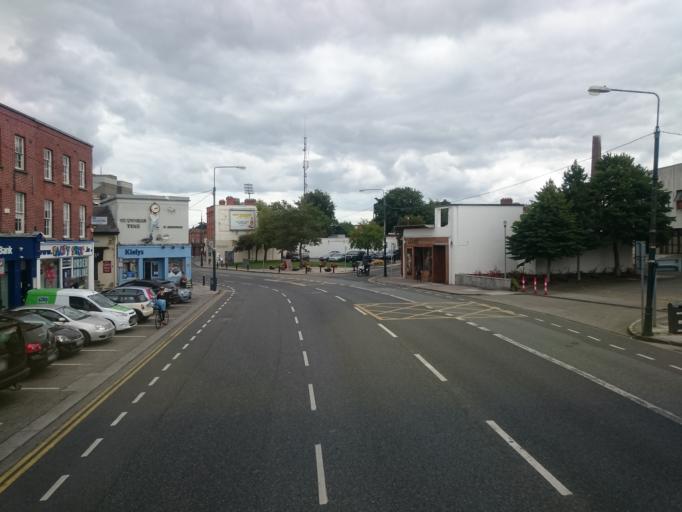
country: IE
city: Clonskeagh
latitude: 53.3224
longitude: -6.2373
